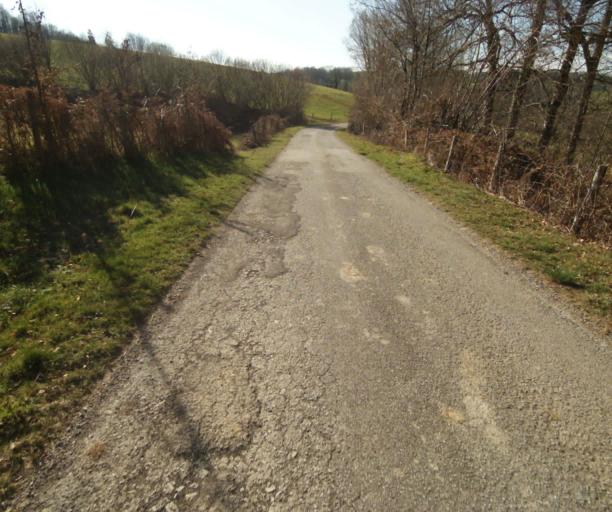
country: FR
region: Limousin
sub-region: Departement de la Correze
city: Chamboulive
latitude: 45.4861
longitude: 1.6947
